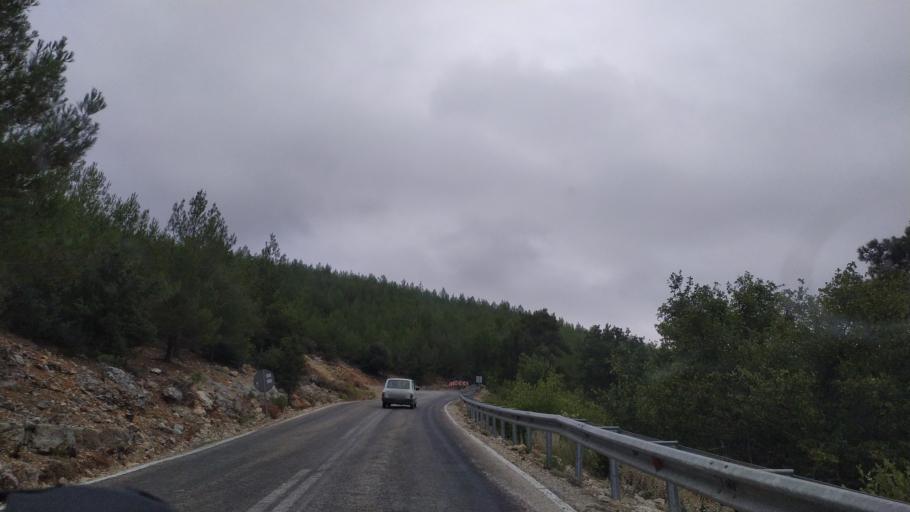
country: TR
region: Mersin
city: Silifke
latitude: 36.5428
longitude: 33.9301
